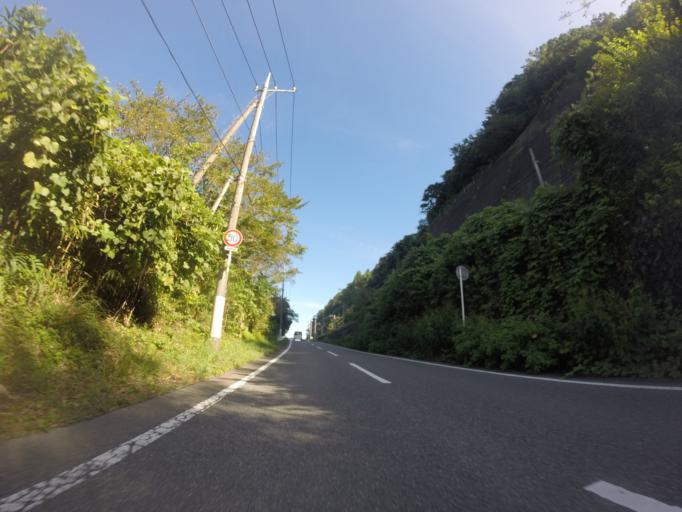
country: JP
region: Shizuoka
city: Fujinomiya
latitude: 35.3043
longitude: 138.4567
